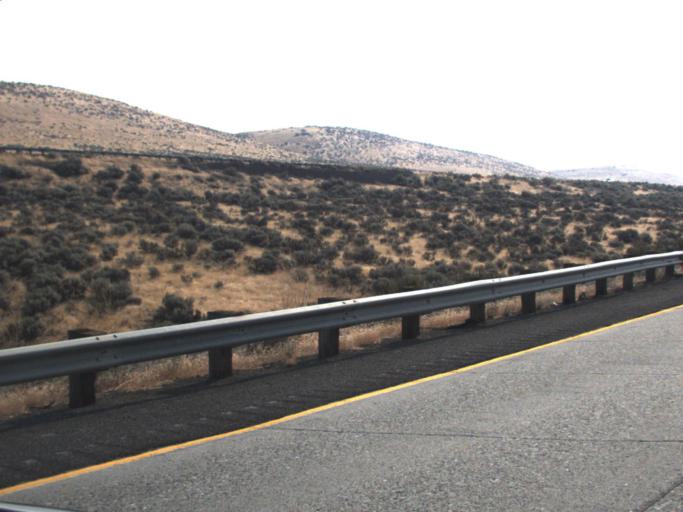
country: US
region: Washington
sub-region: Kittitas County
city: Kittitas
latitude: 46.8485
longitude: -120.3901
